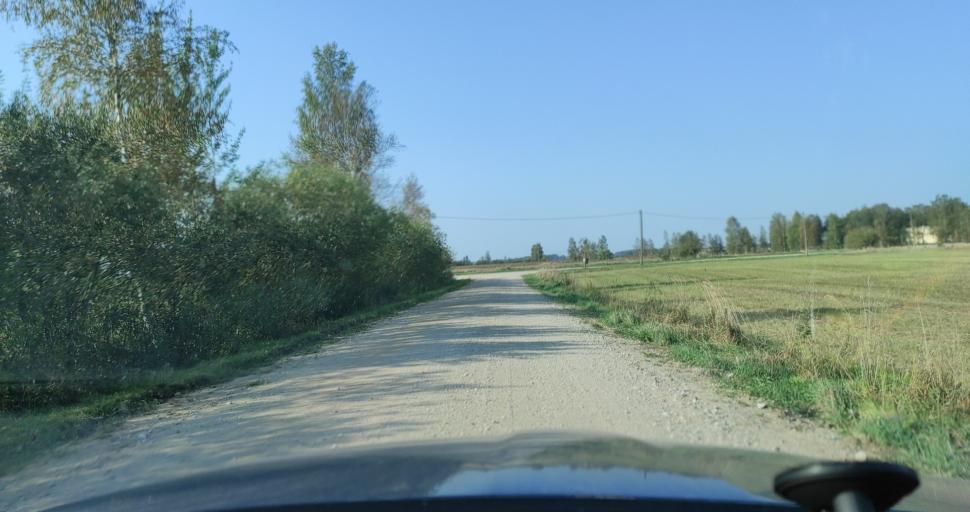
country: LV
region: Ventspils Rajons
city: Piltene
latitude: 57.2233
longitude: 21.6147
